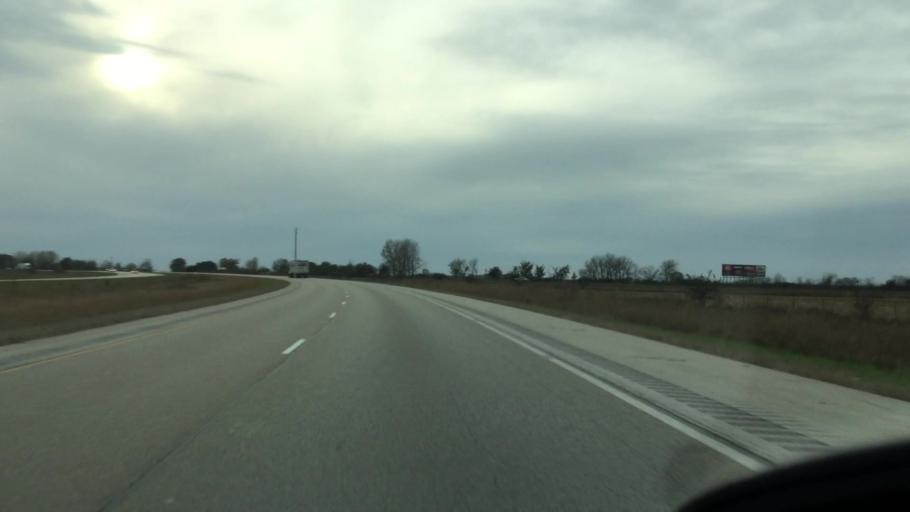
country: US
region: Illinois
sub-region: McLean County
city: Twin Grove
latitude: 40.3956
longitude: -89.0714
